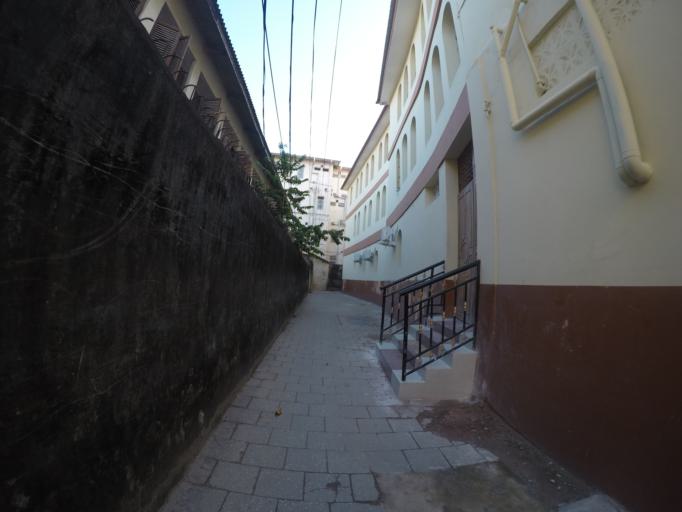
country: TZ
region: Zanzibar Urban/West
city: Zanzibar
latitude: -6.1650
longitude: 39.1918
